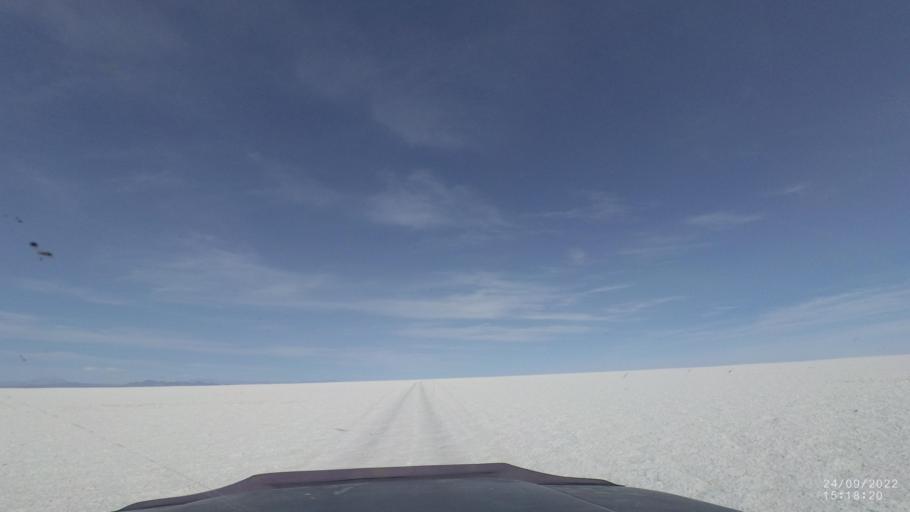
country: BO
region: Potosi
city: Colchani
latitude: -19.9958
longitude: -67.4199
